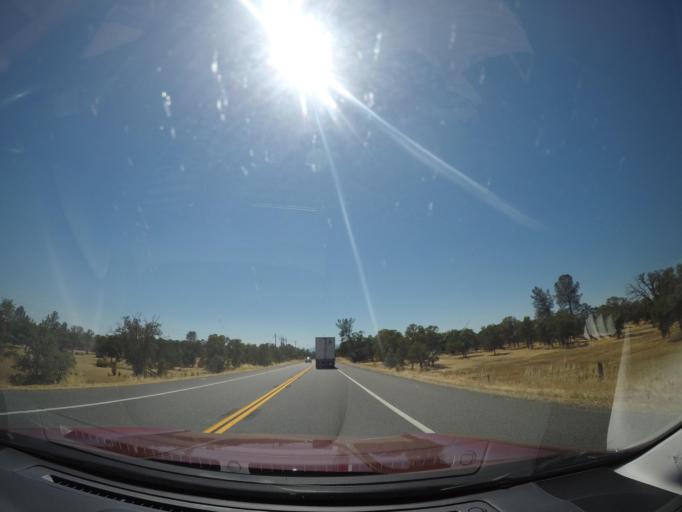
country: US
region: California
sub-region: Shasta County
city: Bella Vista
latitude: 40.6342
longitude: -122.2559
